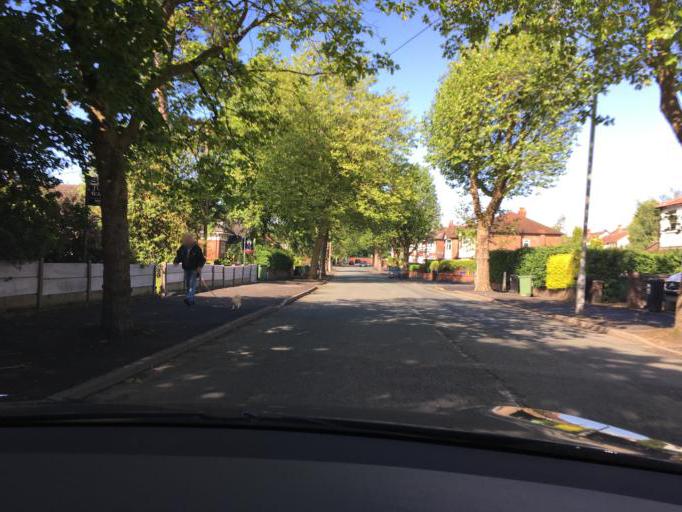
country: GB
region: England
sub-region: Borough of Stockport
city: Hazel Grove
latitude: 53.3929
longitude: -2.1277
